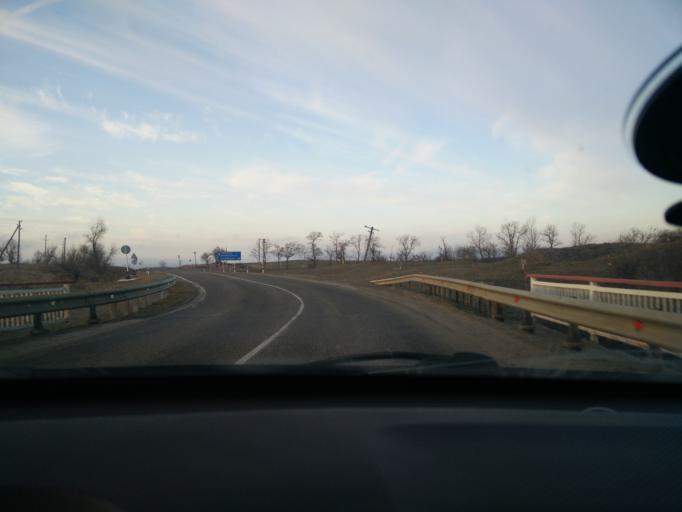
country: RU
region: Stavropol'skiy
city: Balakhonovskoye
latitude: 44.9787
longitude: 41.6879
